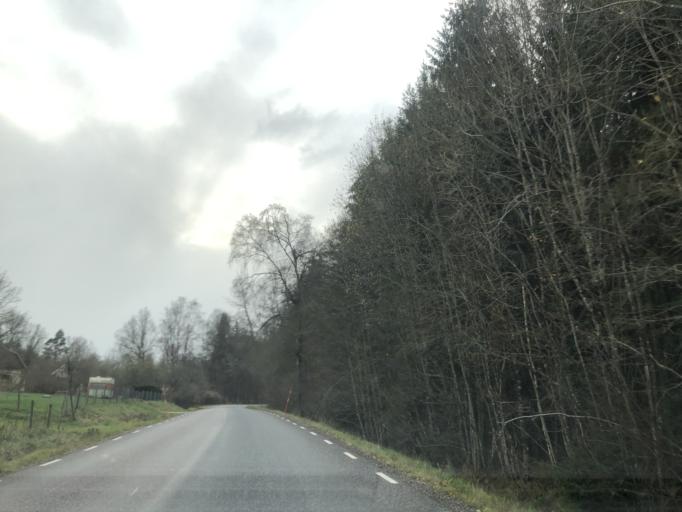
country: SE
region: Vaestra Goetaland
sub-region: Ulricehamns Kommun
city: Ulricehamn
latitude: 57.6762
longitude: 13.4067
